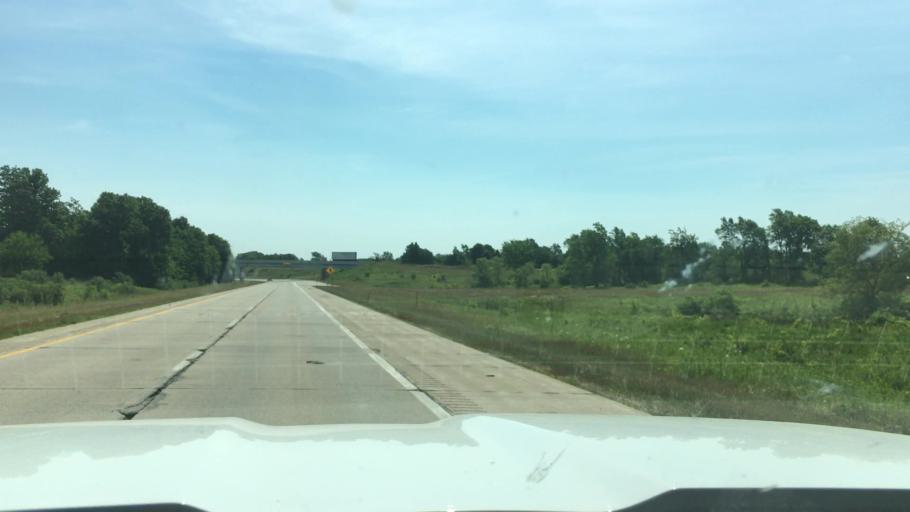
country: US
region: Michigan
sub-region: Clinton County
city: Wacousta
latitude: 42.7882
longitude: -84.6686
